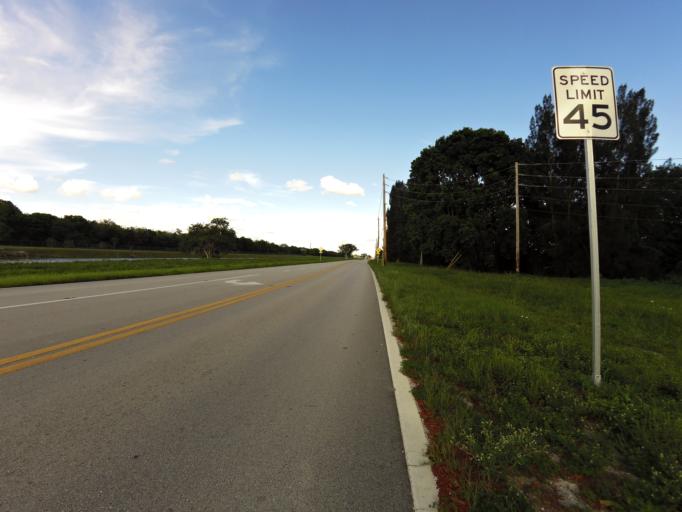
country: US
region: Florida
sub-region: Broward County
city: Weston
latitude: 26.0613
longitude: -80.4144
